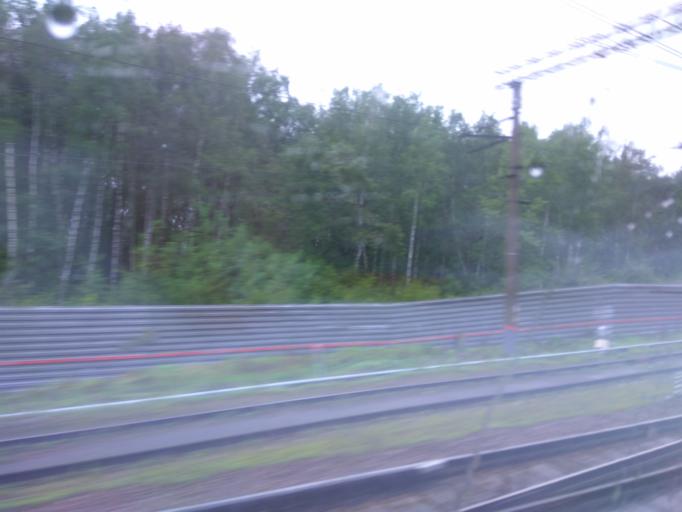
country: RU
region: Moskovskaya
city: Stupino
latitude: 54.9147
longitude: 38.0735
